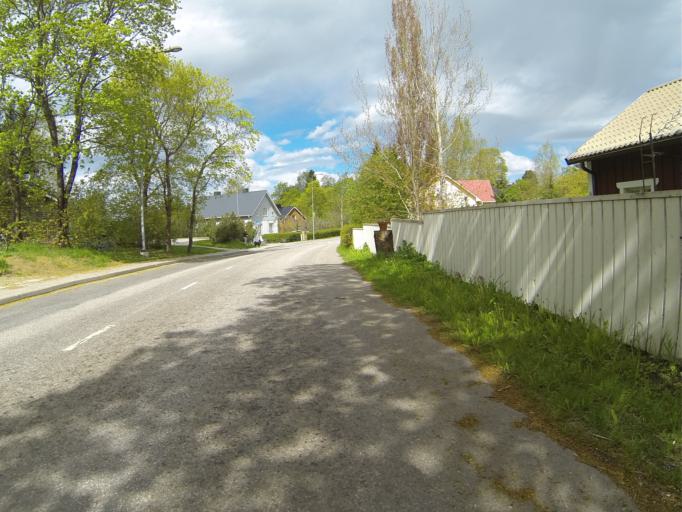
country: FI
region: Varsinais-Suomi
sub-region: Salo
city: Salo
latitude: 60.3781
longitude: 23.1321
